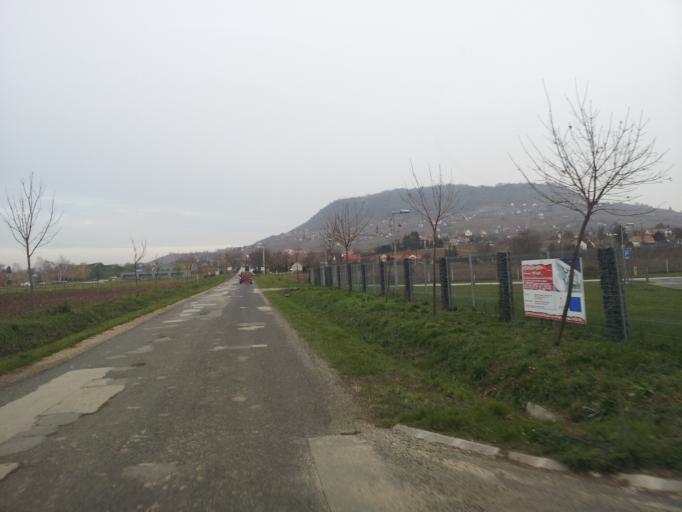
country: HU
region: Veszprem
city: Devecser
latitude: 47.1282
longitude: 17.3734
